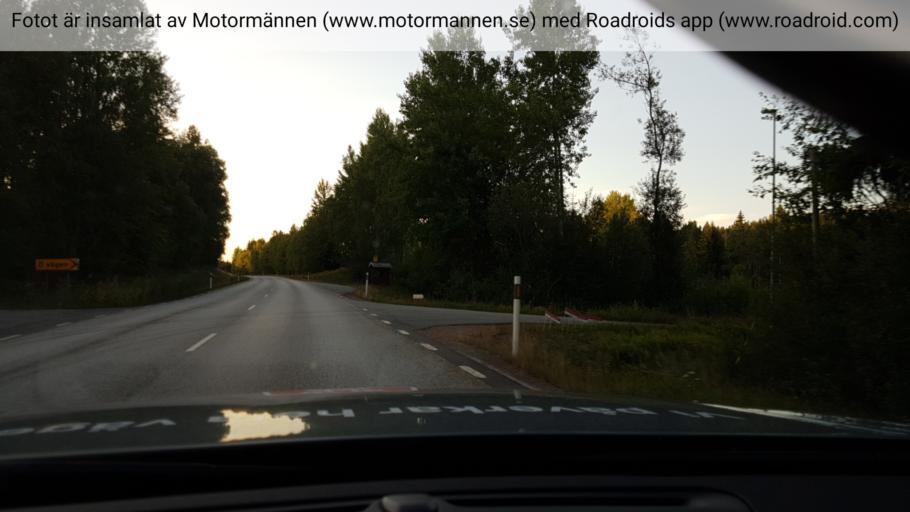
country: SE
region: Vaermland
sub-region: Storfors Kommun
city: Storfors
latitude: 59.5196
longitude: 14.3022
